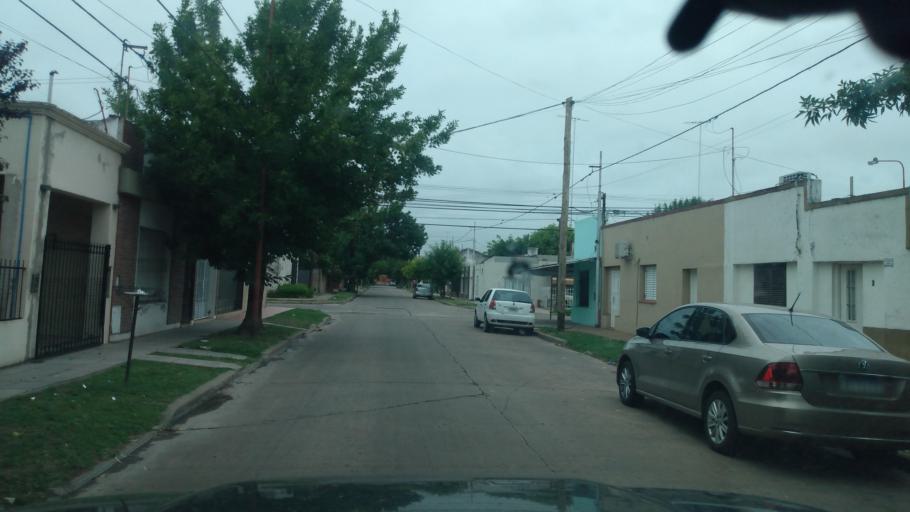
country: AR
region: Buenos Aires
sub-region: Partido de Lujan
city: Lujan
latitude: -34.5725
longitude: -59.1168
